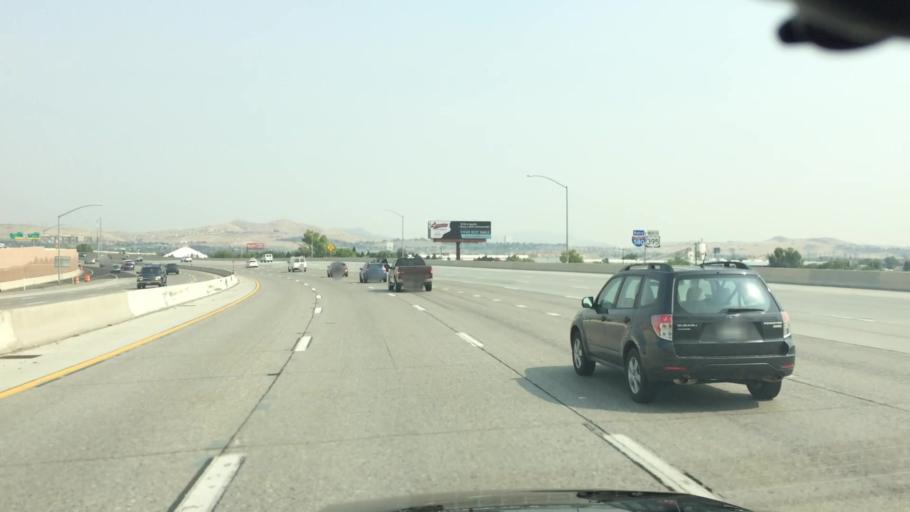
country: US
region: Nevada
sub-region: Washoe County
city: Reno
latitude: 39.5287
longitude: -119.7849
